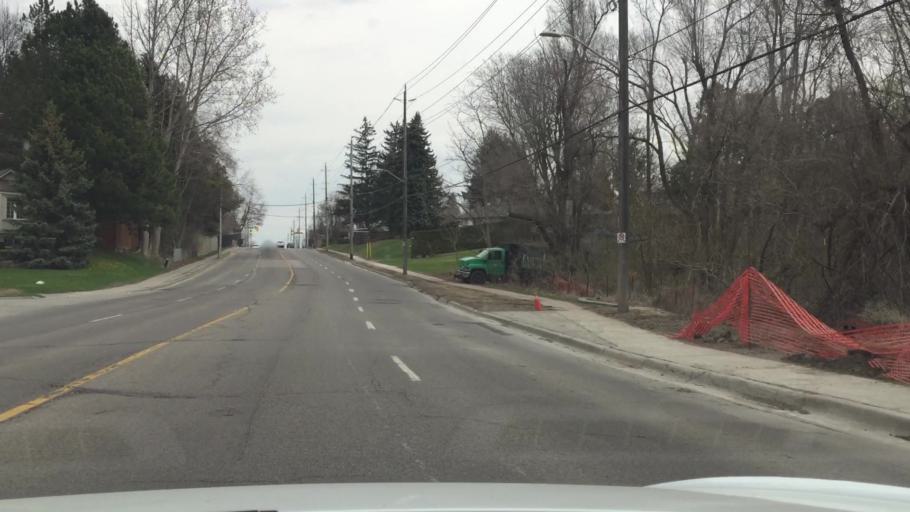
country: CA
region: Ontario
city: Oshawa
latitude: 43.9134
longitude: -78.8789
